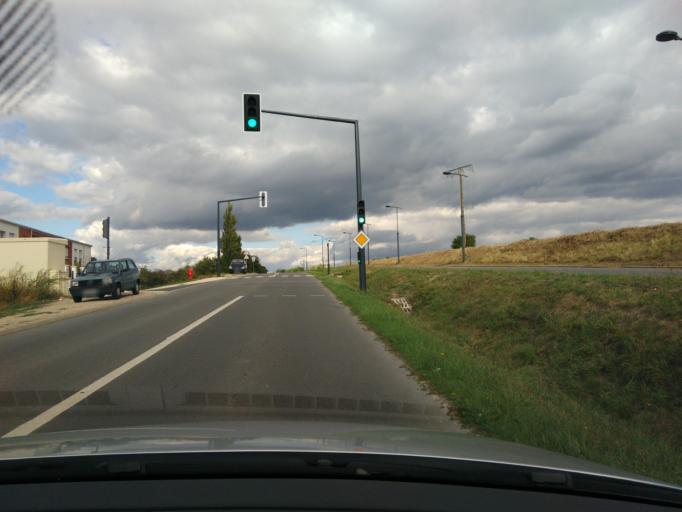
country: FR
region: Ile-de-France
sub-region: Departement de Seine-et-Marne
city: Villenoy
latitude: 48.9343
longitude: 2.8667
